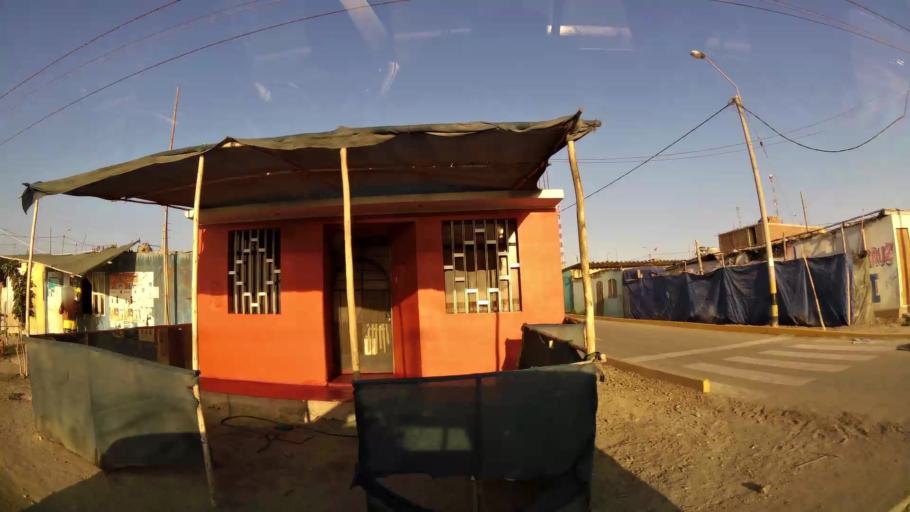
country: PE
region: Ica
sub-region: Provincia de Pisco
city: Villa Tupac Amaru
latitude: -13.7107
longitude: -76.1461
